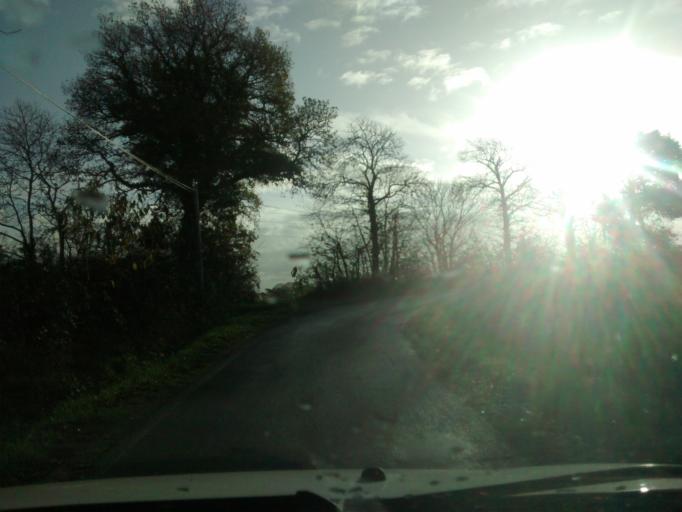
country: FR
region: Brittany
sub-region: Departement d'Ille-et-Vilaine
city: Acigne
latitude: 48.1218
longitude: -1.5623
